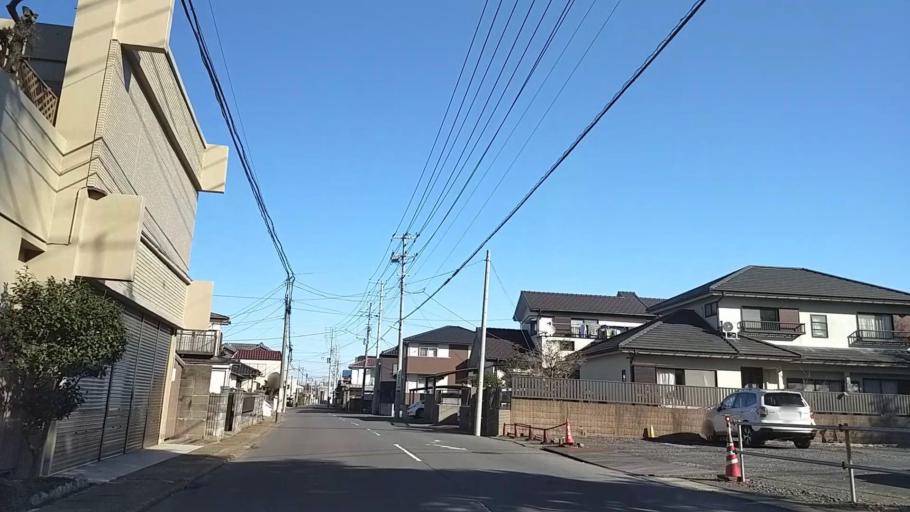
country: JP
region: Chiba
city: Hasaki
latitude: 35.7257
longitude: 140.8351
